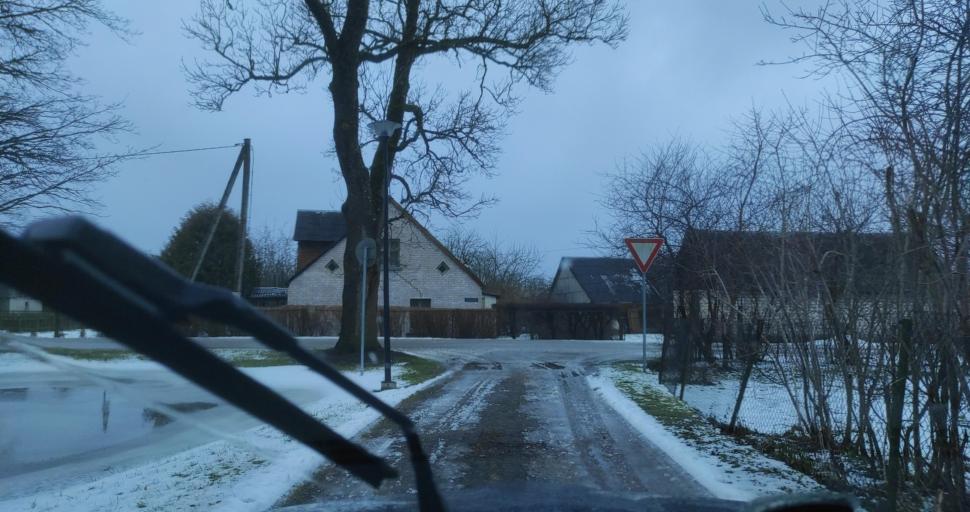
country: LV
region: Dundaga
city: Dundaga
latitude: 57.5146
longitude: 22.0217
